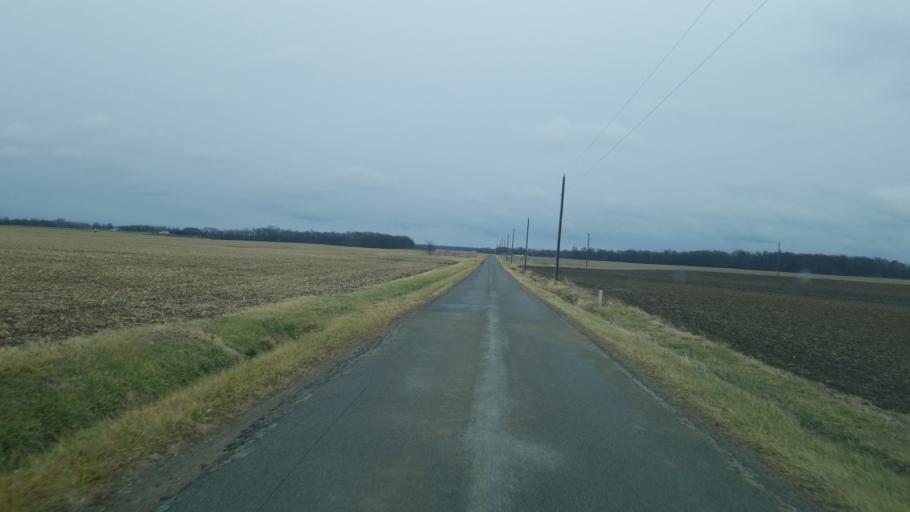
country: US
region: Ohio
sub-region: Union County
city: Marysville
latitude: 40.3095
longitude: -83.3164
